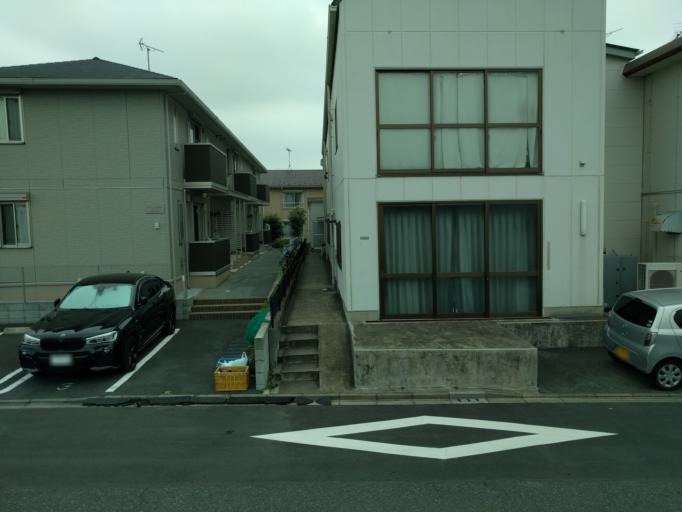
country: JP
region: Kanagawa
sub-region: Kawasaki-shi
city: Kawasaki
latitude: 35.5939
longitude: 139.6539
